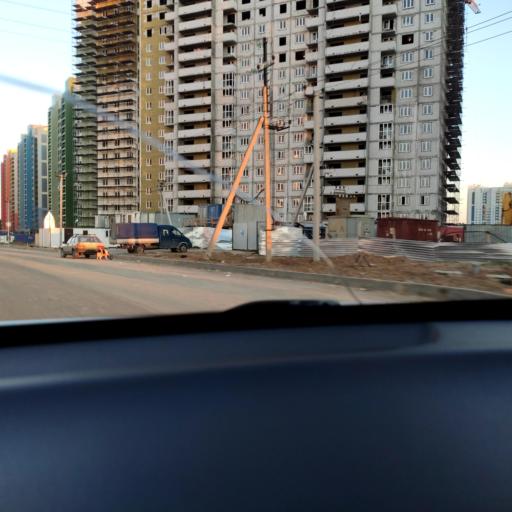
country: RU
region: Tatarstan
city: Osinovo
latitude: 55.8594
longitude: 48.9017
